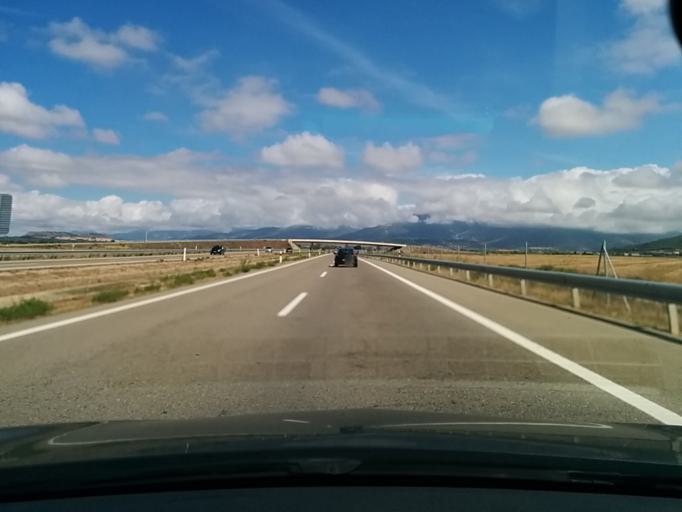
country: ES
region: Aragon
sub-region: Provincia de Huesca
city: Banastas
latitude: 42.1890
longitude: -0.4327
